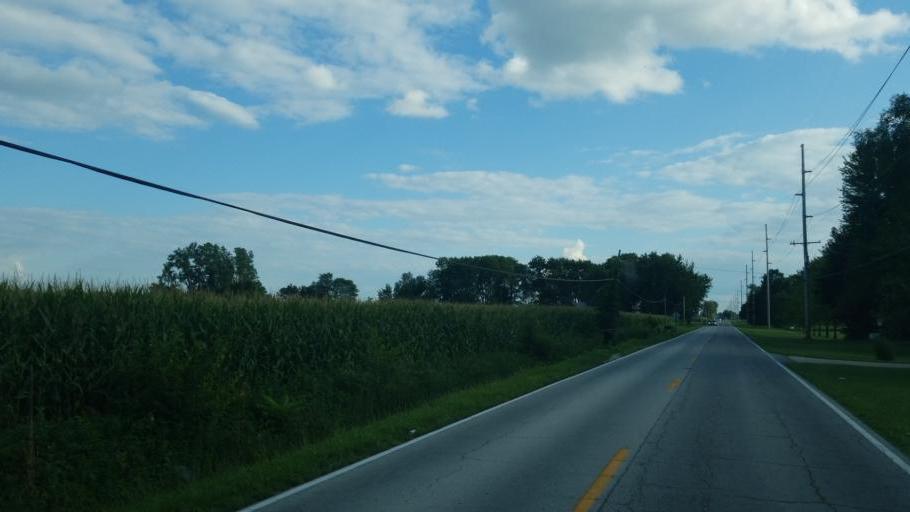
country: US
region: Ohio
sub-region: Sandusky County
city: Ballville
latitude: 41.3118
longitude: -83.1300
